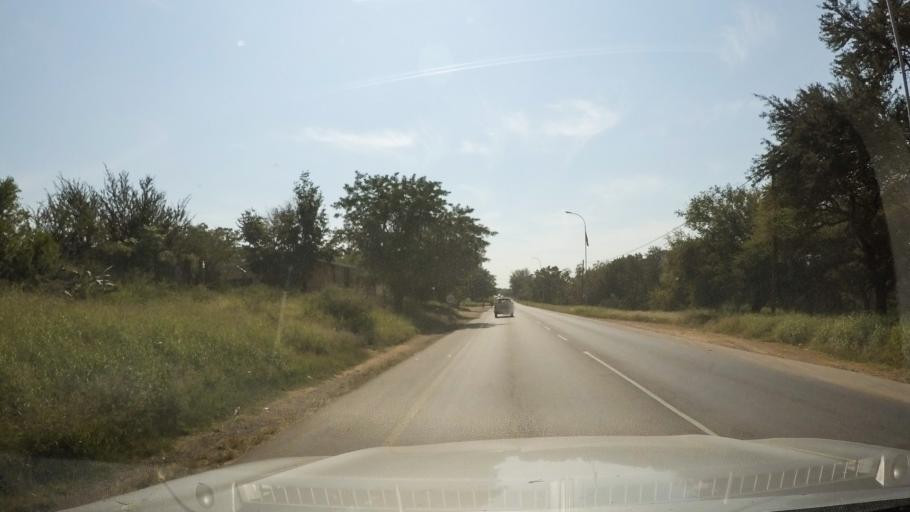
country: BW
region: South East
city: Lobatse
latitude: -25.2249
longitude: 25.6774
